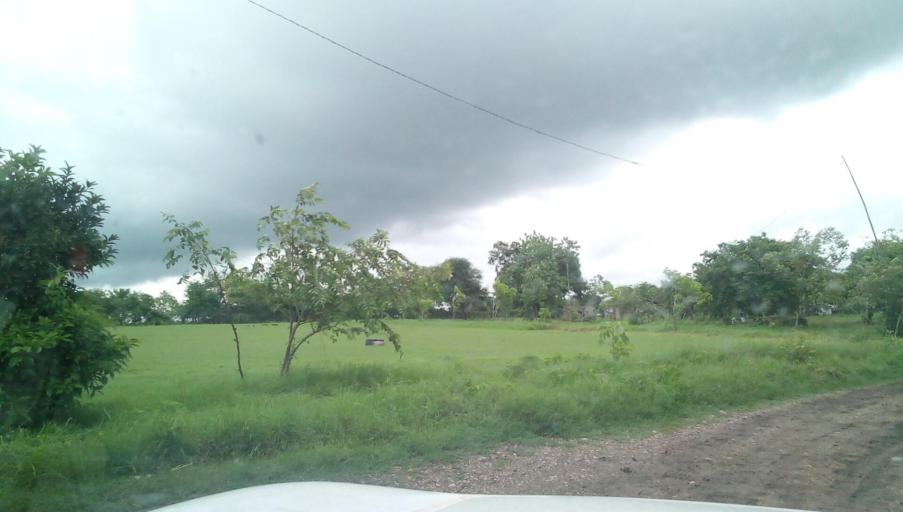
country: MX
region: Veracruz
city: Panuco
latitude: 21.7994
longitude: -98.0988
